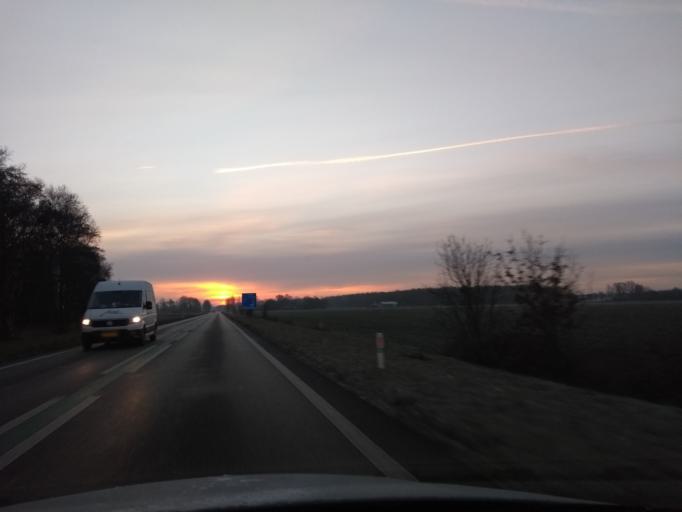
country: NL
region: Friesland
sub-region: Gemeente Gaasterlan-Sleat
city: Balk
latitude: 52.8862
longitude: 5.5920
